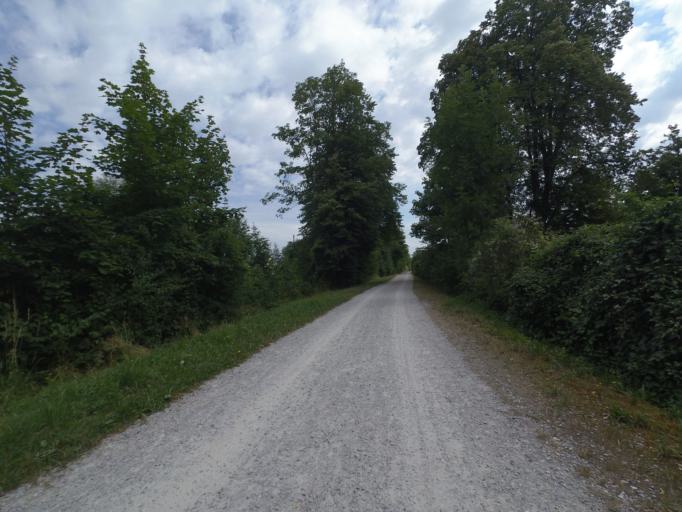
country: DE
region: Bavaria
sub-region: Upper Bavaria
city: Ainring
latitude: 47.7891
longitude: 12.9501
